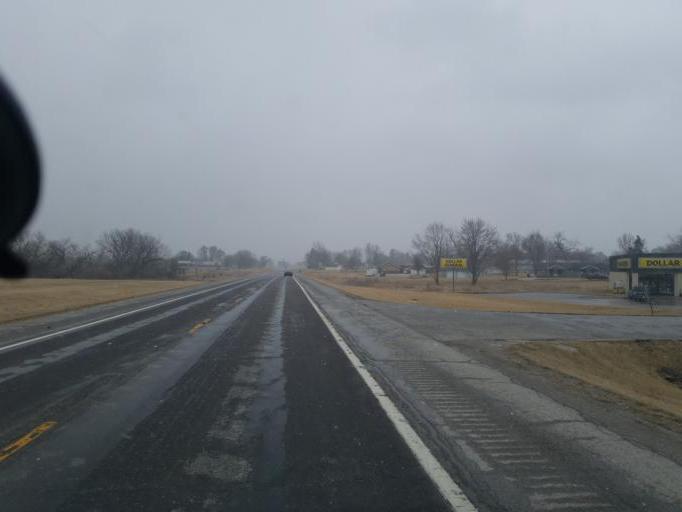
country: US
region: Missouri
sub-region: Schuyler County
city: Lancaster
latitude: 40.4161
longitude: -92.5654
